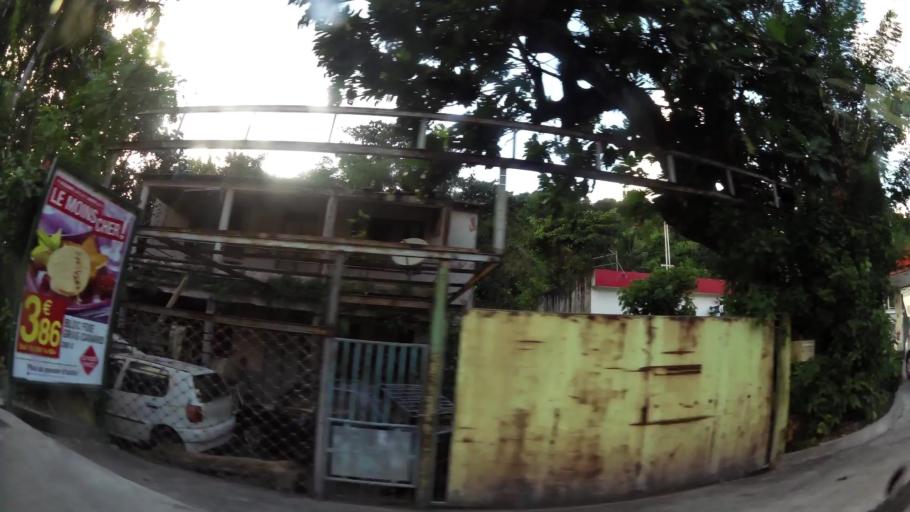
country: MQ
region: Martinique
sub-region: Martinique
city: Fort-de-France
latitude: 14.6176
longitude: -61.0713
